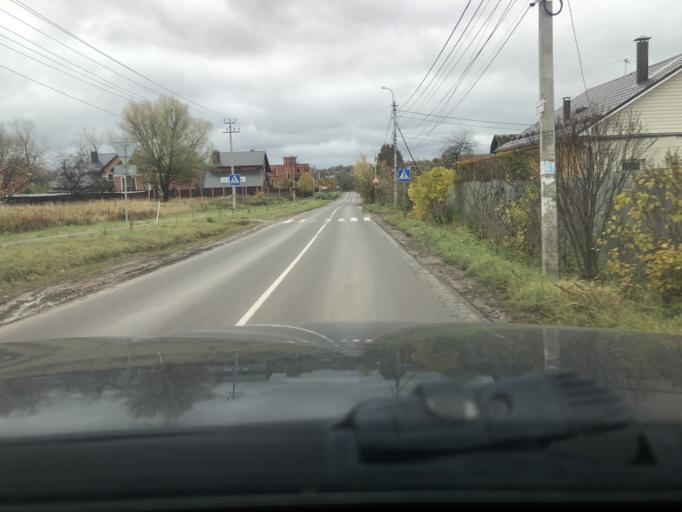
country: RU
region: Moskovskaya
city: Sergiyev Posad
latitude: 56.3056
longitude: 38.1094
